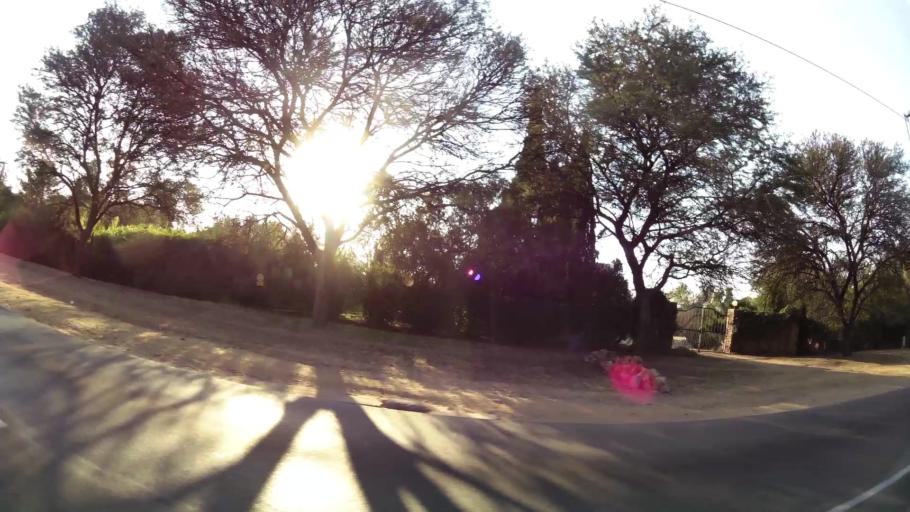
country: ZA
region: Gauteng
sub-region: City of Johannesburg Metropolitan Municipality
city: Midrand
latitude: -26.0255
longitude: 28.1492
